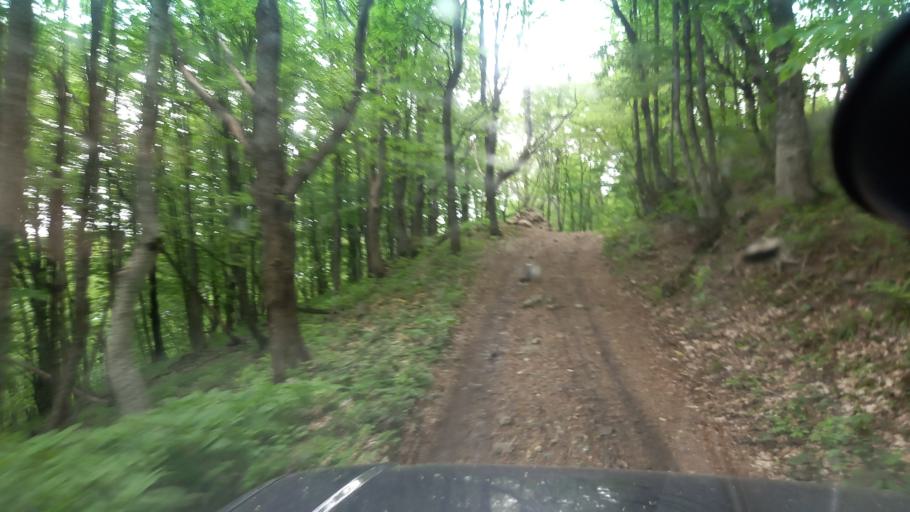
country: RU
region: Krasnodarskiy
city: Tuapse
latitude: 44.2499
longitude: 39.2810
